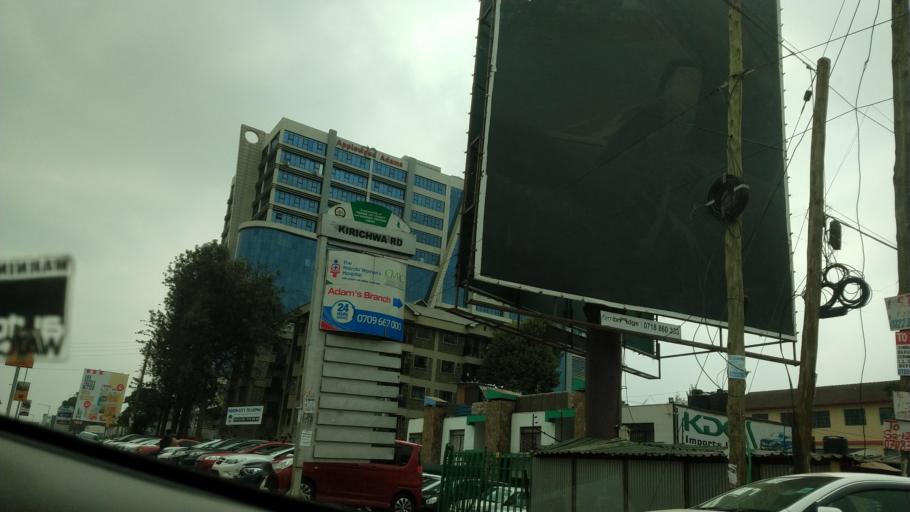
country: KE
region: Nairobi Area
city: Nairobi
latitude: -1.2997
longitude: 36.7821
